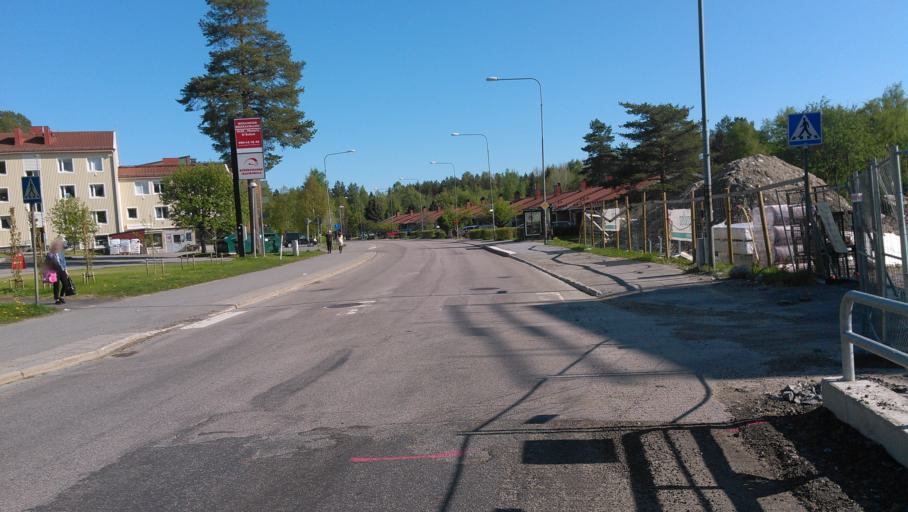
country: SE
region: Vaesterbotten
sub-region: Umea Kommun
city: Umea
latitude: 63.8257
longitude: 20.2945
